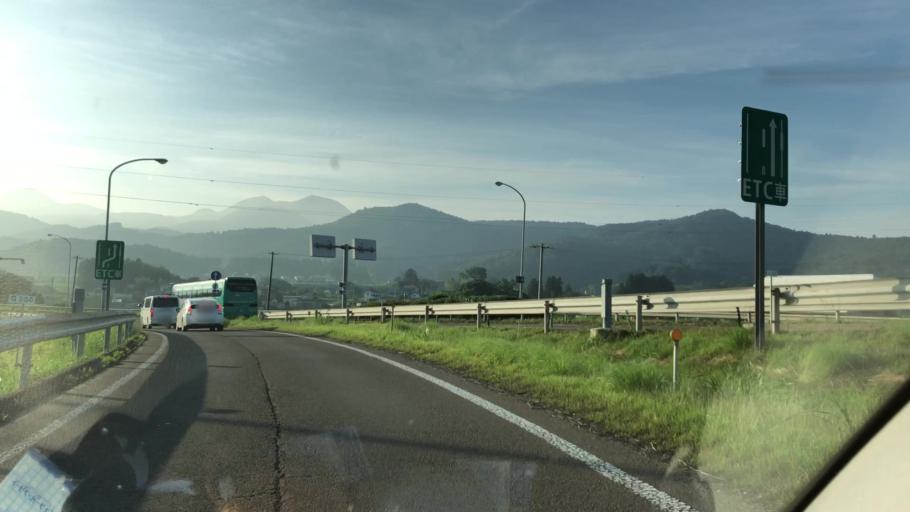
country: JP
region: Miyagi
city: Shiroishi
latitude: 38.0367
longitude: 140.6398
